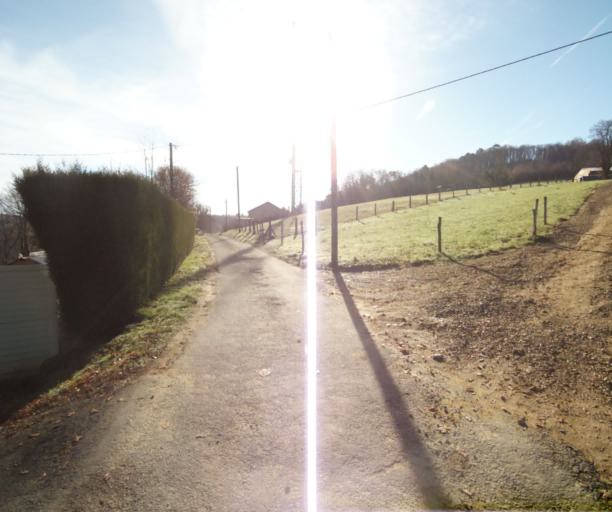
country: FR
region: Limousin
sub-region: Departement de la Correze
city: Laguenne
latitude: 45.2445
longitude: 1.7683
